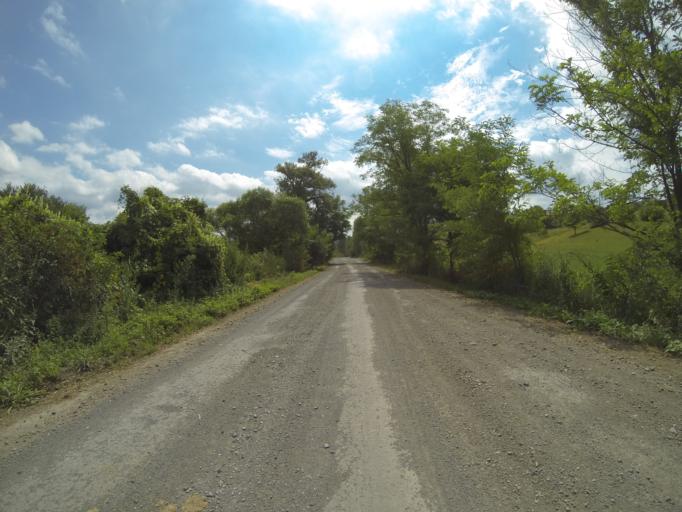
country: RO
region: Brasov
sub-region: Comuna Hoghiz
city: Hoghiz
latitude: 45.9790
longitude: 25.3640
